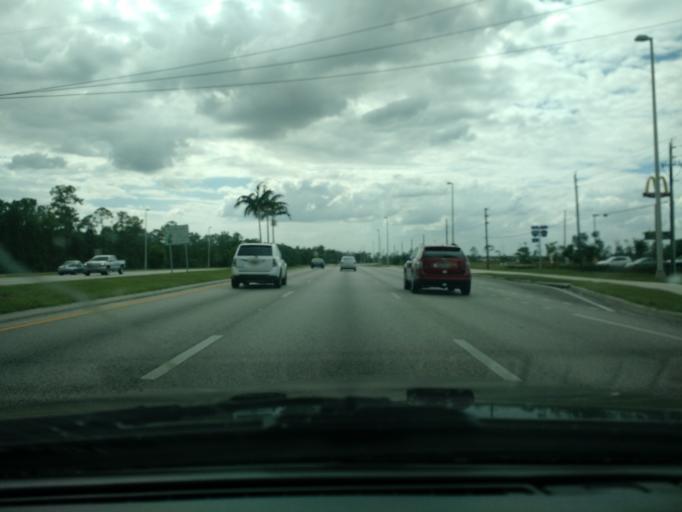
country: US
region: Florida
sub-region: Lee County
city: Gateway
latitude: 26.6183
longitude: -81.7685
